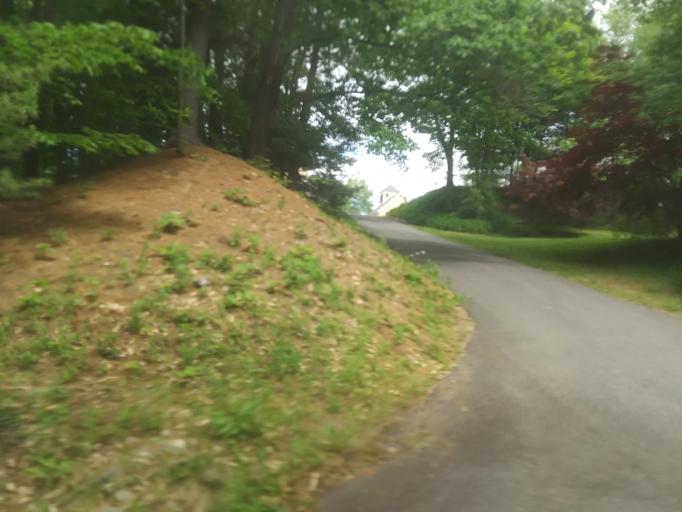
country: US
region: Massachusetts
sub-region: Franklin County
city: Shelburne Falls
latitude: 42.6124
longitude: -72.7624
